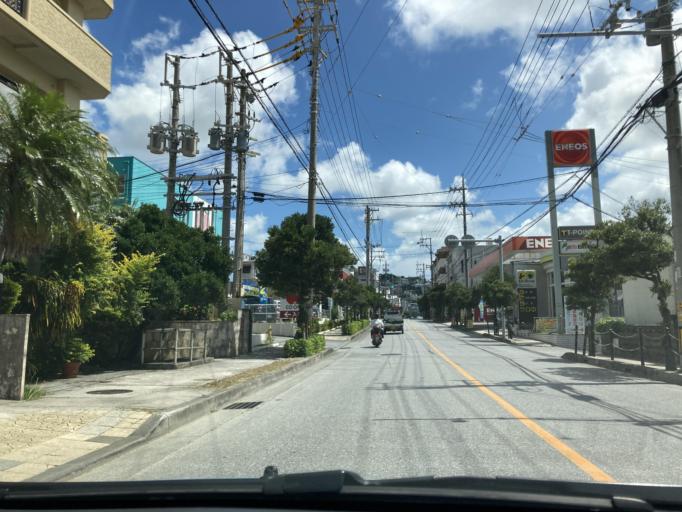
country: JP
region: Okinawa
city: Naha-shi
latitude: 26.2170
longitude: 127.7075
